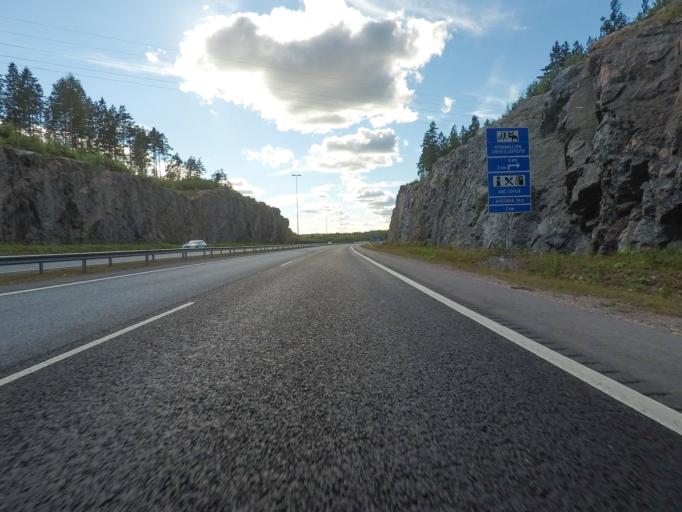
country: FI
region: Uusimaa
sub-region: Helsinki
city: Lohja
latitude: 60.2830
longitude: 24.1027
